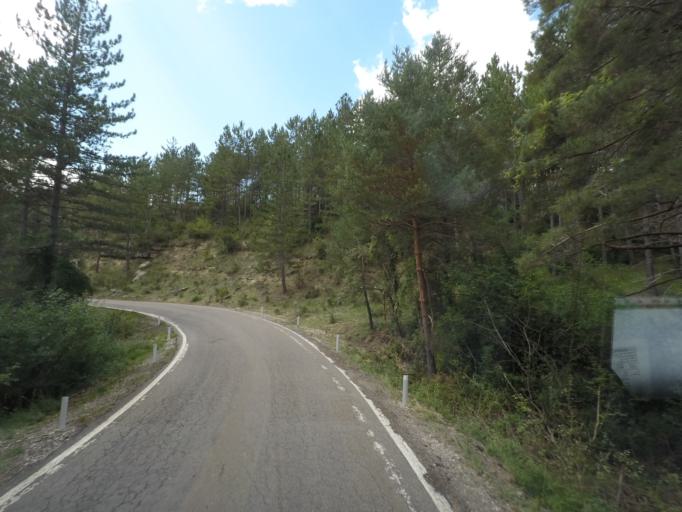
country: ES
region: Aragon
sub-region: Provincia de Huesca
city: Fiscal
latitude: 42.4094
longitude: -0.1583
